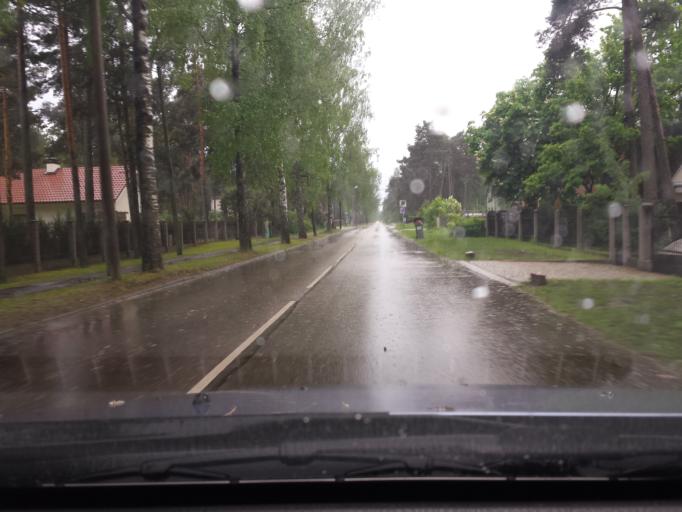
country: LV
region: Riga
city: Bolderaja
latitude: 57.0718
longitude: 24.1047
